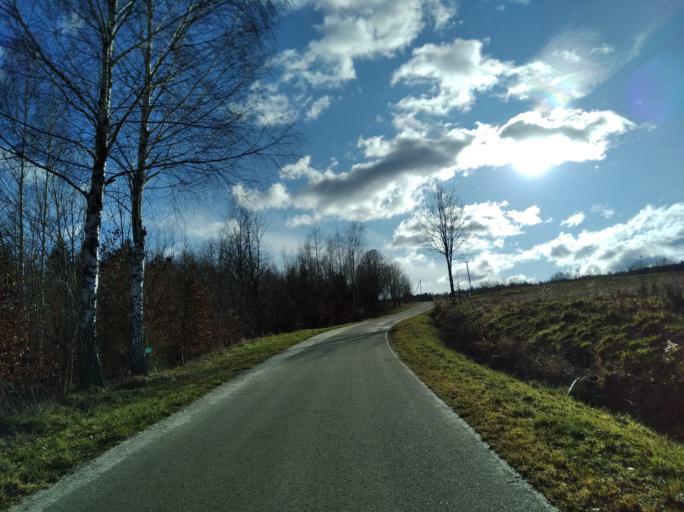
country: PL
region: Subcarpathian Voivodeship
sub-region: Powiat strzyzowski
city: Wisniowa
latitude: 49.9001
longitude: 21.6868
